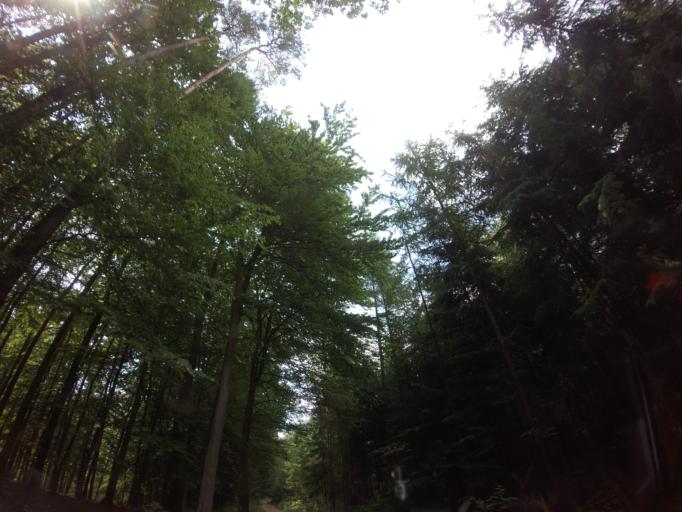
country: PL
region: West Pomeranian Voivodeship
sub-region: Powiat choszczenski
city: Bierzwnik
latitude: 53.0702
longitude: 15.6745
